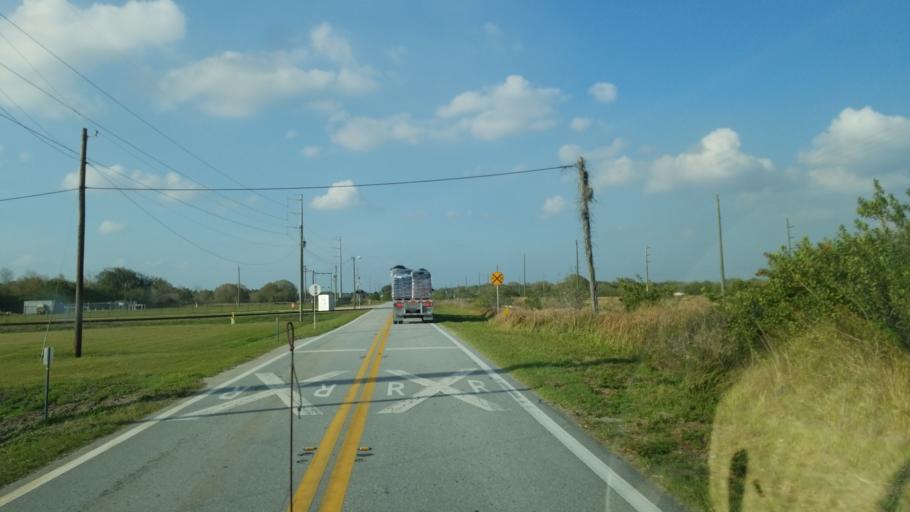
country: US
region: Florida
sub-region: Hardee County
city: Bowling Green
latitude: 27.6849
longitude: -81.9558
